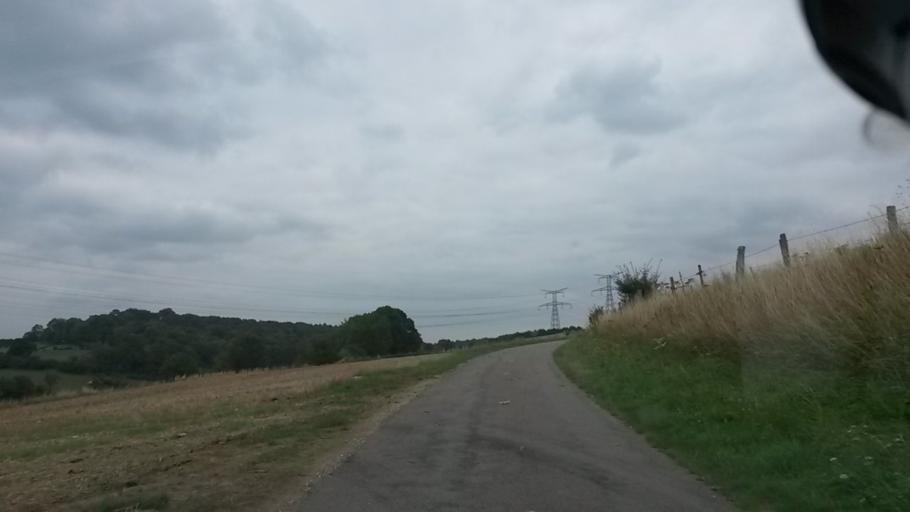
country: FR
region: Haute-Normandie
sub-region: Departement de la Seine-Maritime
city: La Feuillie
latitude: 49.4796
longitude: 1.5200
